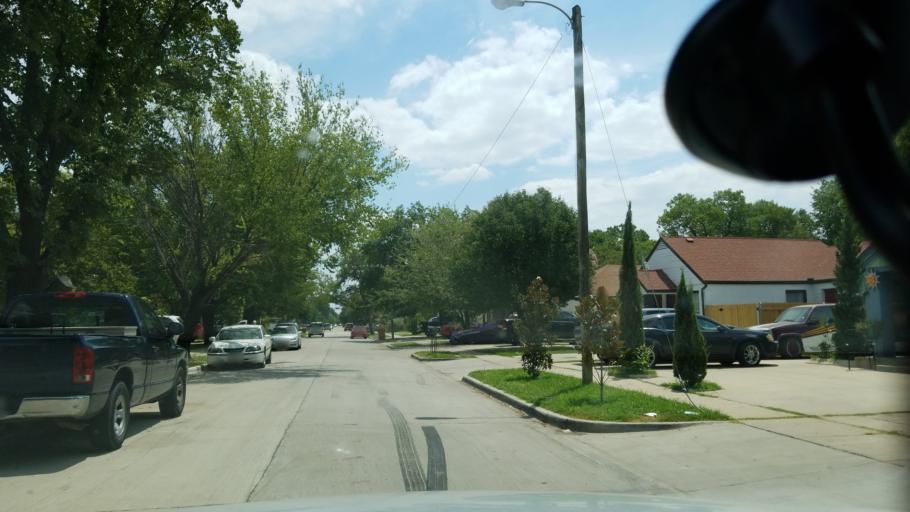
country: US
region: Texas
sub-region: Dallas County
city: Grand Prairie
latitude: 32.7496
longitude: -96.9875
